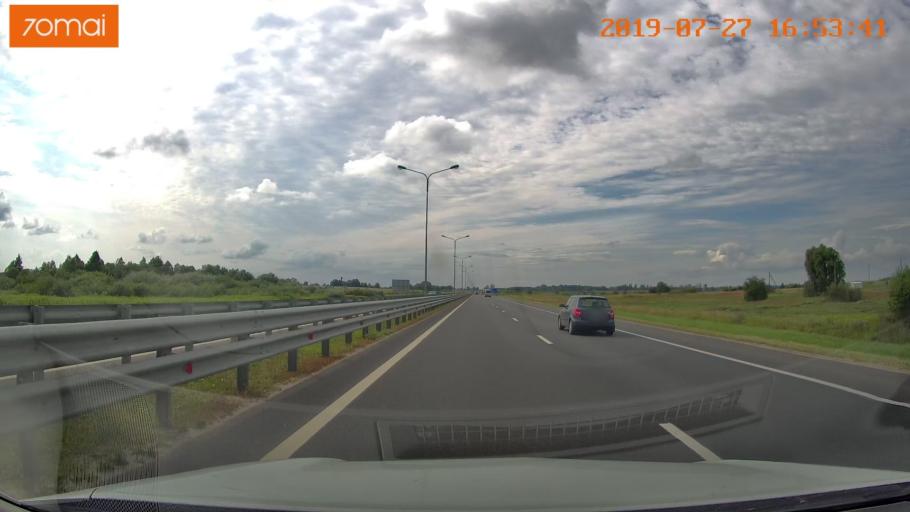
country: RU
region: Kaliningrad
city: Bol'shoe Isakovo
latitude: 54.6895
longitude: 20.8272
